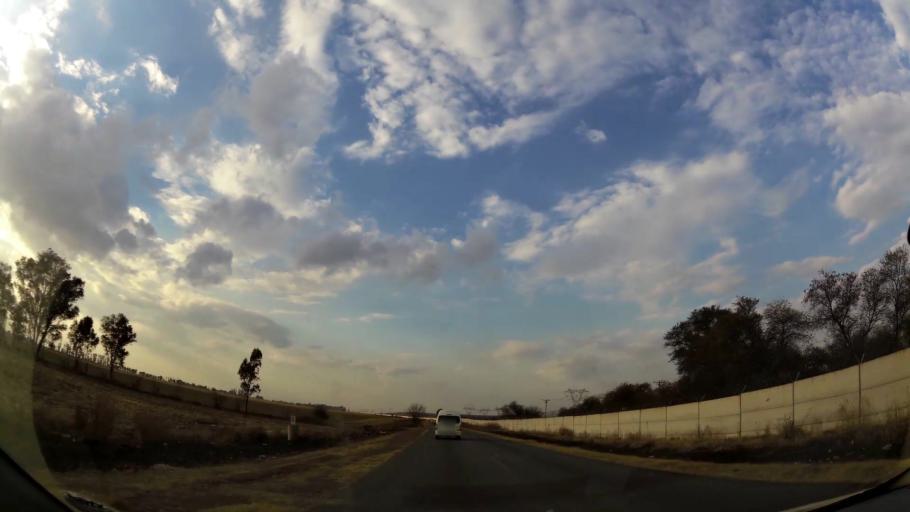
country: ZA
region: Gauteng
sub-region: Sedibeng District Municipality
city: Vanderbijlpark
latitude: -26.6608
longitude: 27.7993
